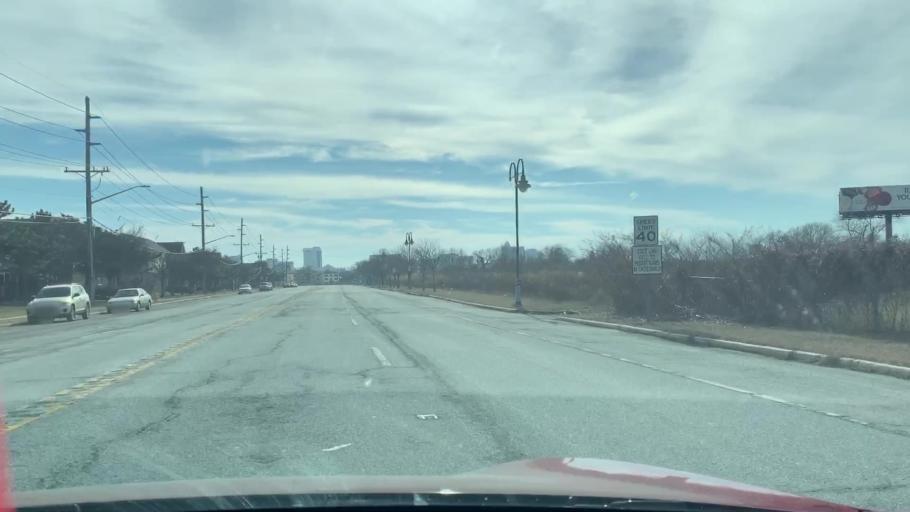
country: US
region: New Jersey
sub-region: Atlantic County
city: Atlantic City
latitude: 39.3755
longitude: -74.4313
